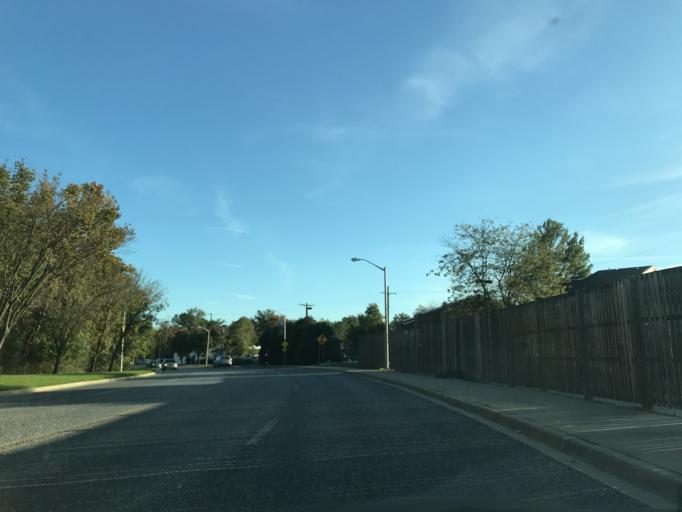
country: US
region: Maryland
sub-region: Prince George's County
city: College Park
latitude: 38.9854
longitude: -76.9332
